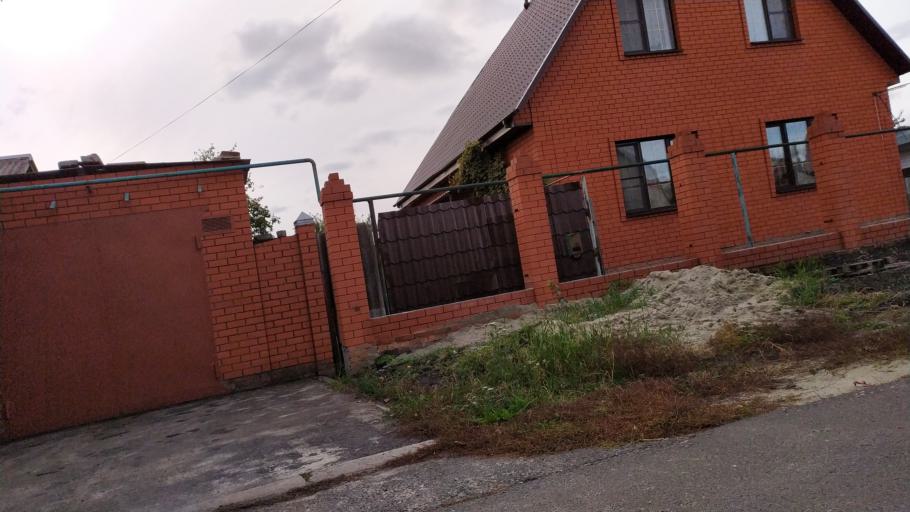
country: RU
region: Kursk
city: Kursk
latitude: 51.6462
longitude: 36.1509
